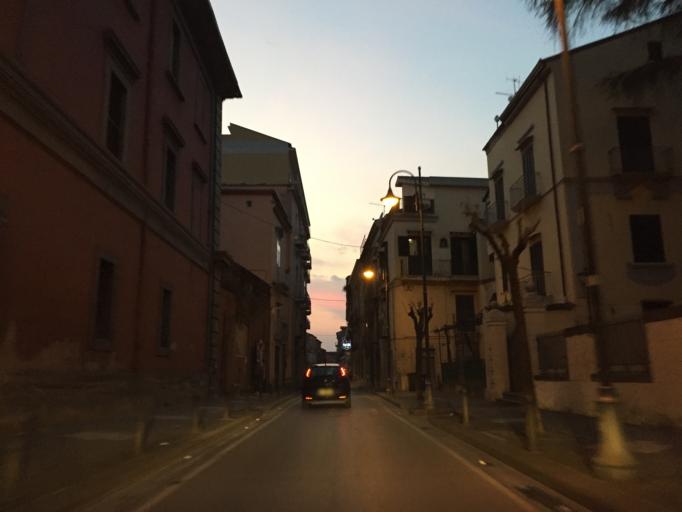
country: IT
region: Campania
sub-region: Provincia di Salerno
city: Nocera Inferiore
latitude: 40.7470
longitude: 14.6426
